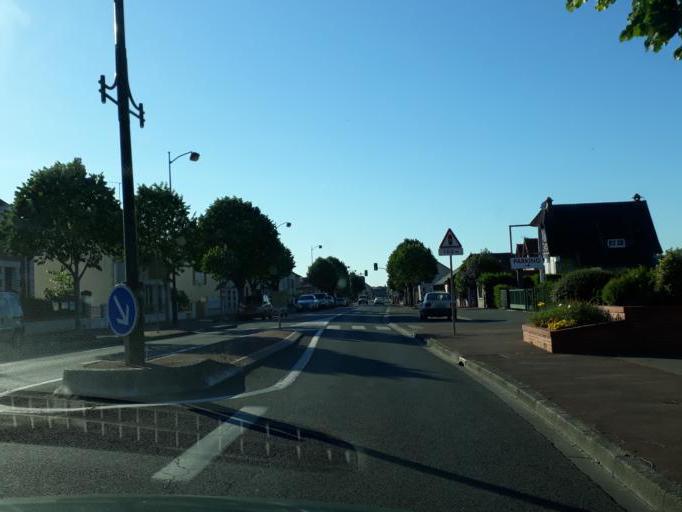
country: FR
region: Centre
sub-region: Departement du Loiret
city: Briare
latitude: 47.6341
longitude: 2.7443
